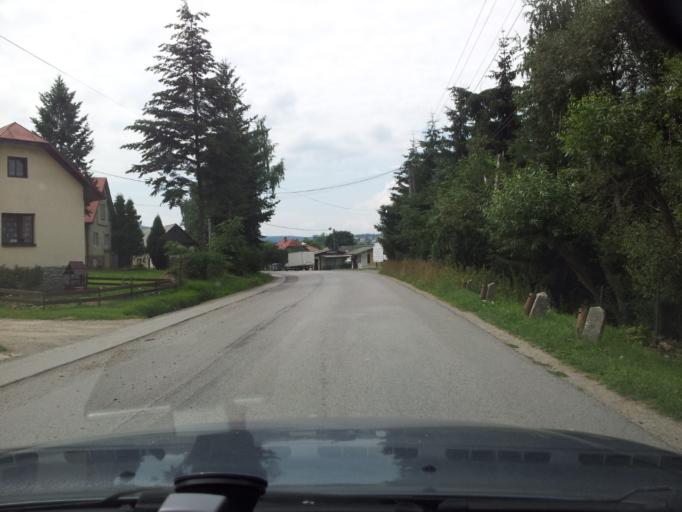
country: SK
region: Zilinsky
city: Oravska Lesna
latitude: 49.3850
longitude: 19.2966
